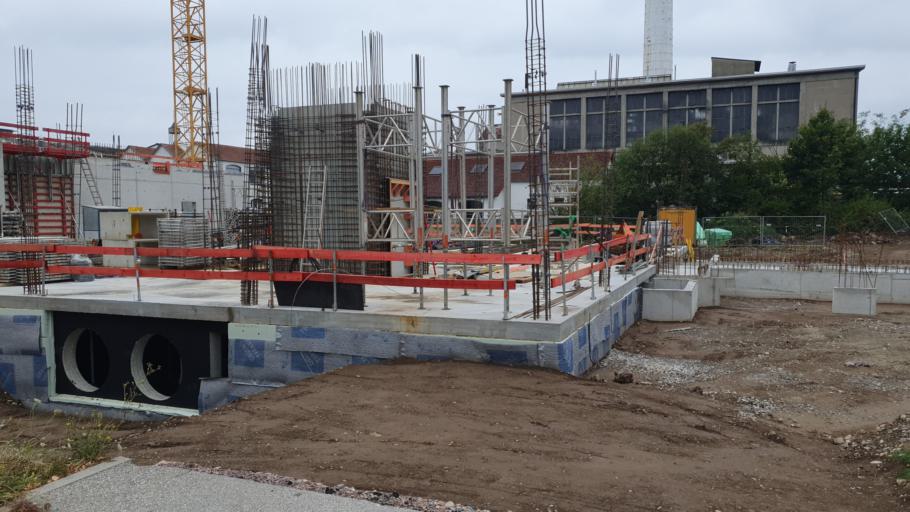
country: DE
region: Baden-Wuerttemberg
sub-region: Freiburg Region
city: Loerrach
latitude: 47.6106
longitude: 7.6562
